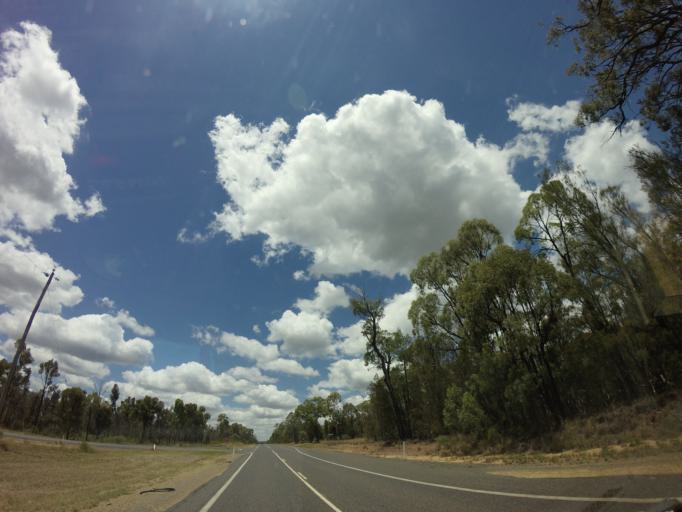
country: AU
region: Queensland
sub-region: Western Downs
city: Dalby
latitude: -27.9823
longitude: 150.9771
